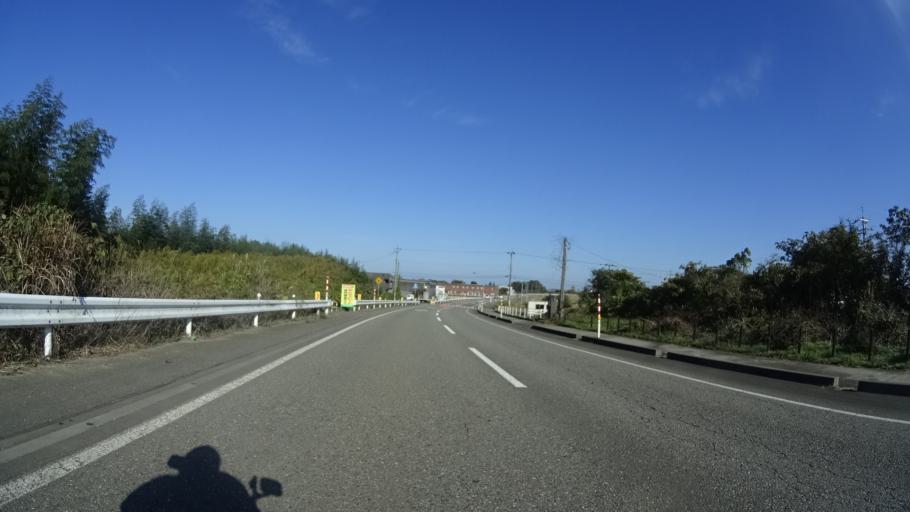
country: JP
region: Ishikawa
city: Komatsu
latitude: 36.3042
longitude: 136.3854
